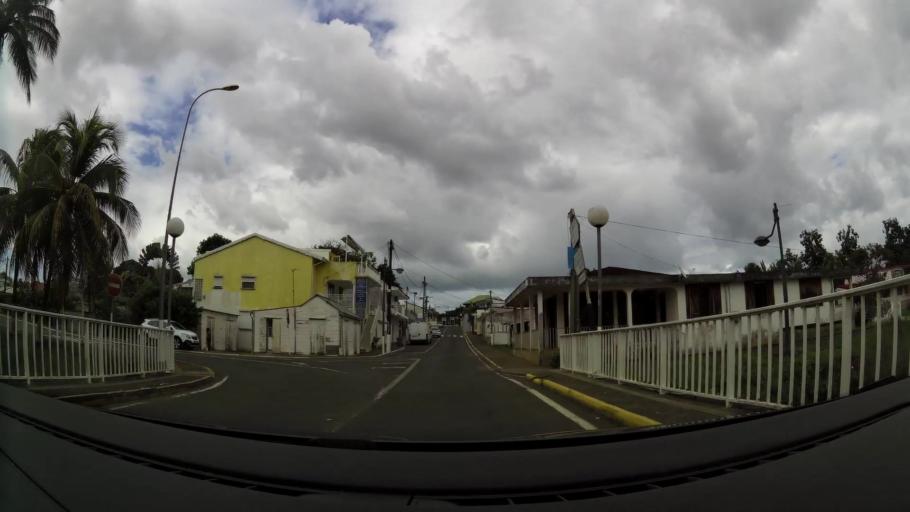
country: GP
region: Guadeloupe
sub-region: Guadeloupe
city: Lamentin
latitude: 16.2703
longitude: -61.6316
